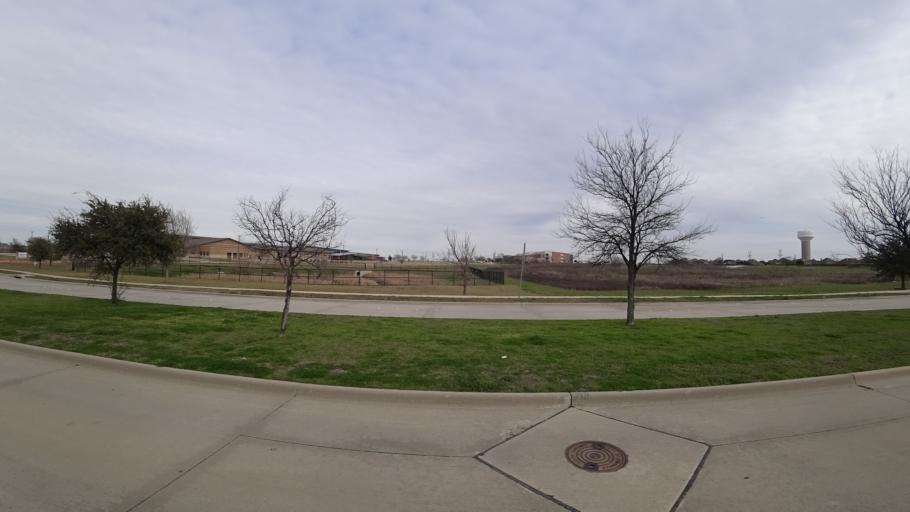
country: US
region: Texas
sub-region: Denton County
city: The Colony
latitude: 33.0490
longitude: -96.9131
